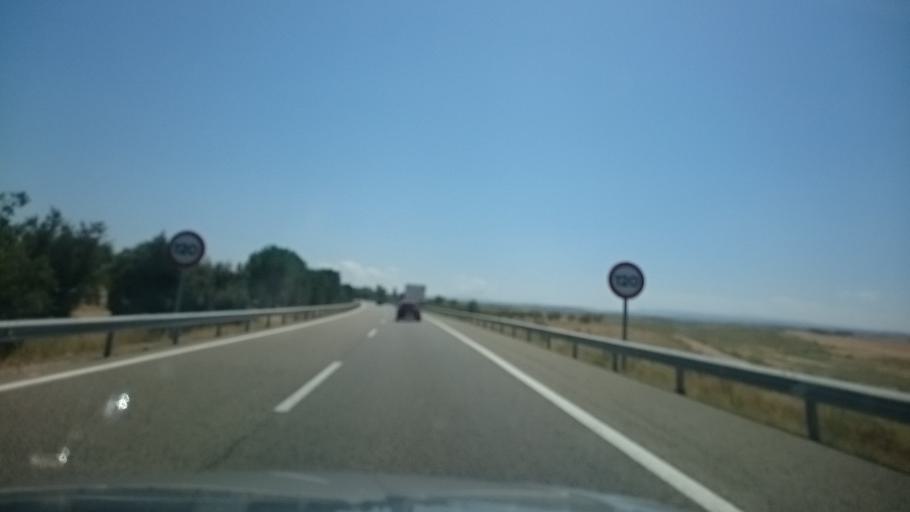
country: ES
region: Catalonia
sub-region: Provincia de Lleida
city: Alfes
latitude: 41.5448
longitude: 0.6307
